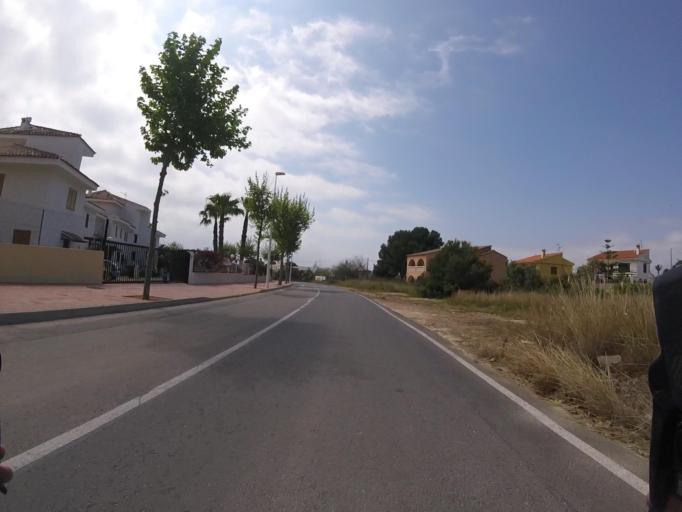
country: ES
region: Valencia
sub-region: Provincia de Castello
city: Alcoceber
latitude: 40.2452
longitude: 0.2705
